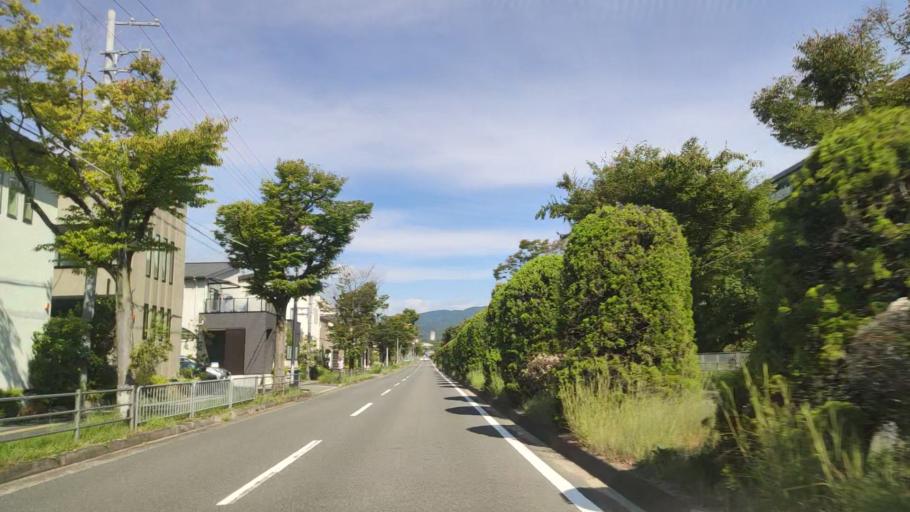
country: JP
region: Osaka
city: Mino
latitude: 34.8139
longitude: 135.5145
